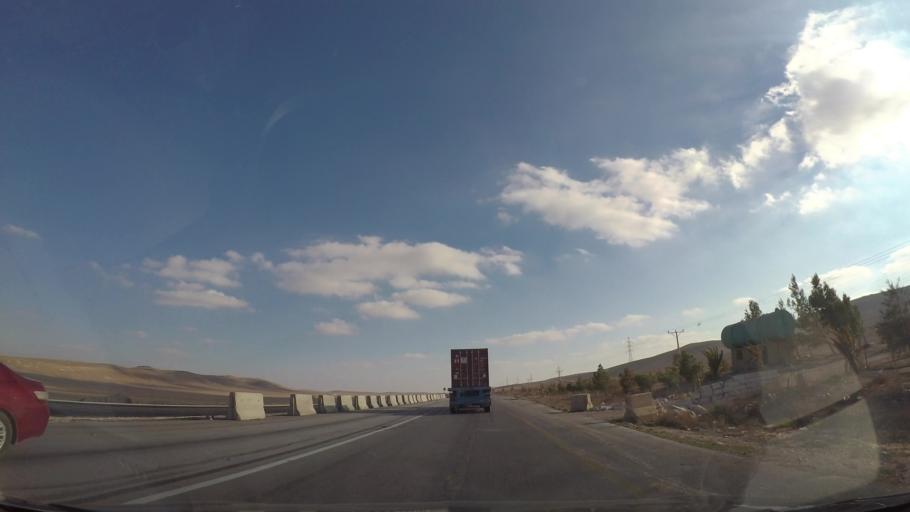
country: JO
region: Karak
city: Adir
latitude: 31.1886
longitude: 36.0178
